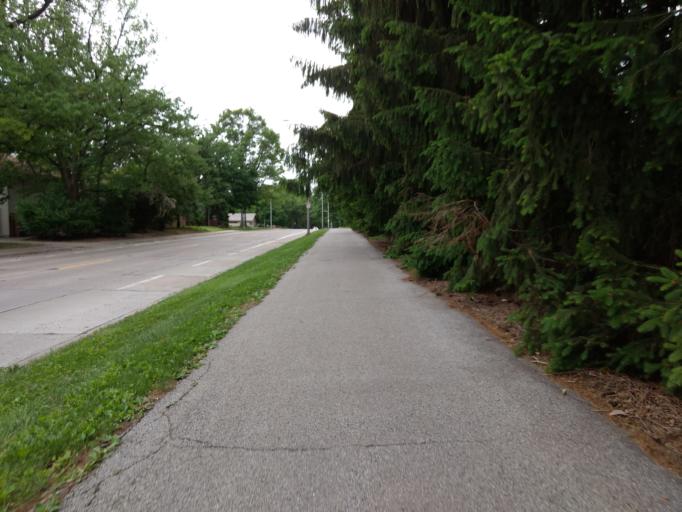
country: US
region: Illinois
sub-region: Champaign County
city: Urbana
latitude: 40.0965
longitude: -88.2097
